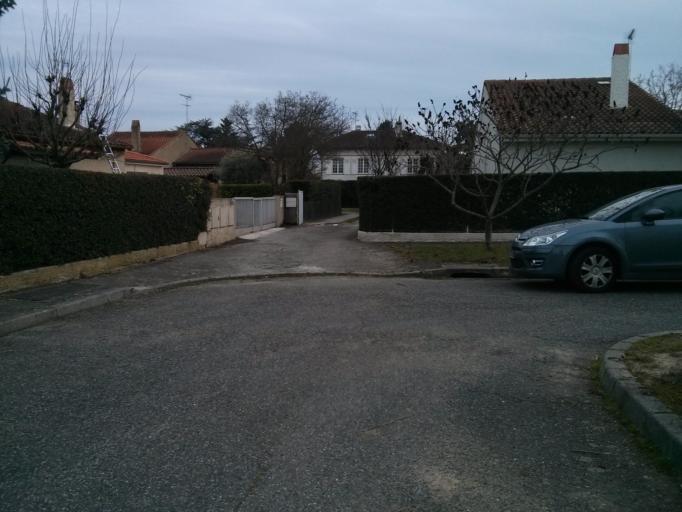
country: FR
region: Midi-Pyrenees
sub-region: Departement de la Haute-Garonne
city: Castanet-Tolosan
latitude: 43.5144
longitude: 1.5085
